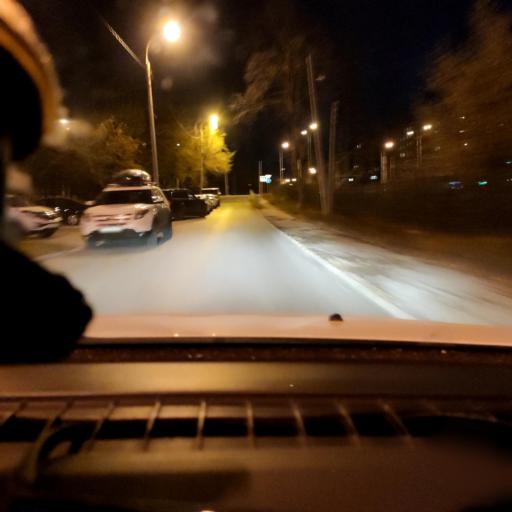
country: RU
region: Samara
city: Samara
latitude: 53.2476
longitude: 50.2019
